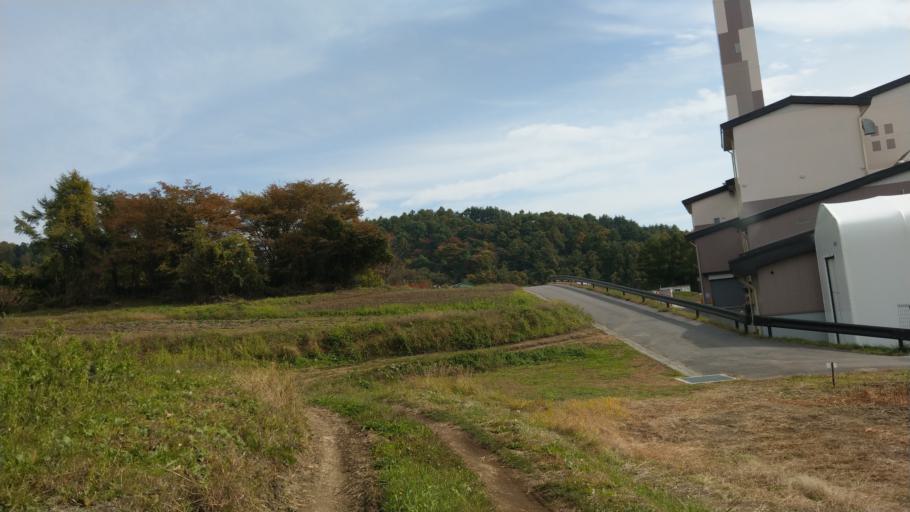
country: JP
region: Nagano
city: Komoro
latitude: 36.3501
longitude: 138.4360
